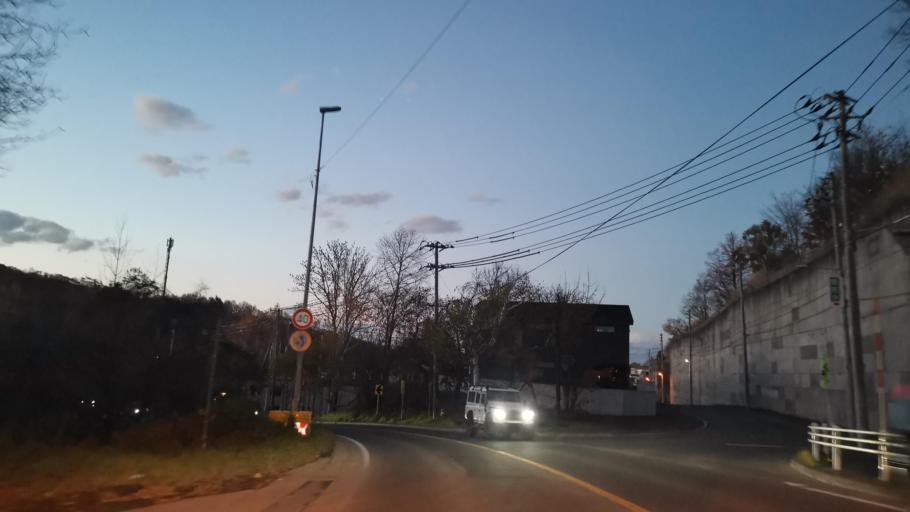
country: JP
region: Hokkaido
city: Sapporo
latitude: 42.9939
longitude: 141.3660
